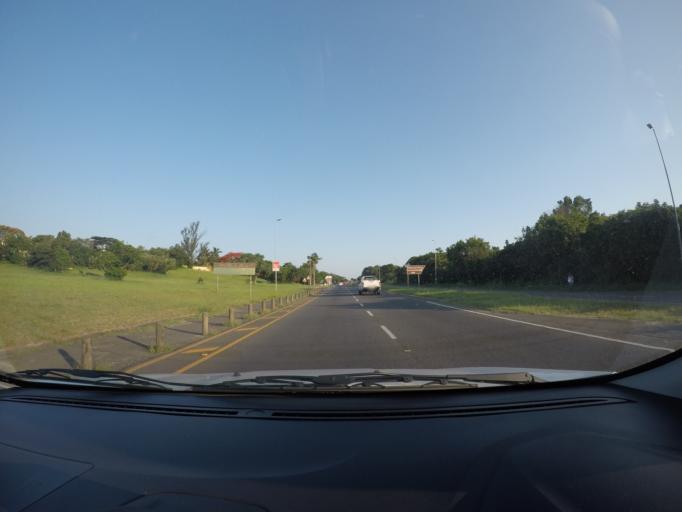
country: ZA
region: KwaZulu-Natal
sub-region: uThungulu District Municipality
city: Richards Bay
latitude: -28.7861
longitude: 32.0888
